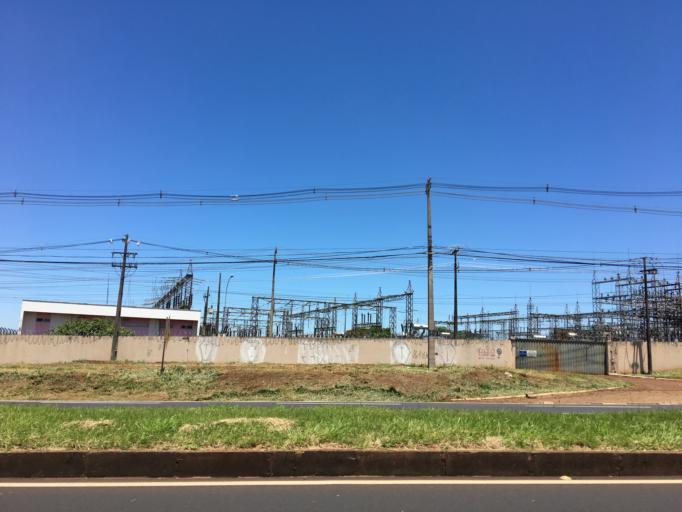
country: BR
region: Parana
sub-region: Maringa
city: Maringa
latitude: -23.4494
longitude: -51.9858
